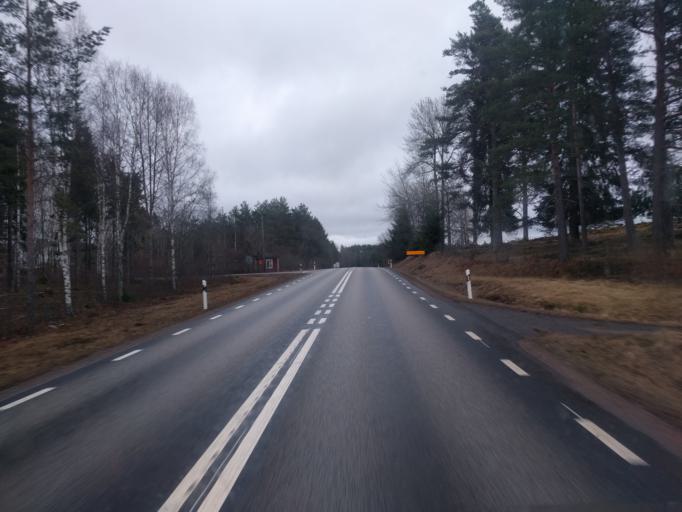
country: SE
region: Joenkoeping
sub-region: Eksjo Kommun
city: Haljarp
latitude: 57.6208
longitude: 15.4749
